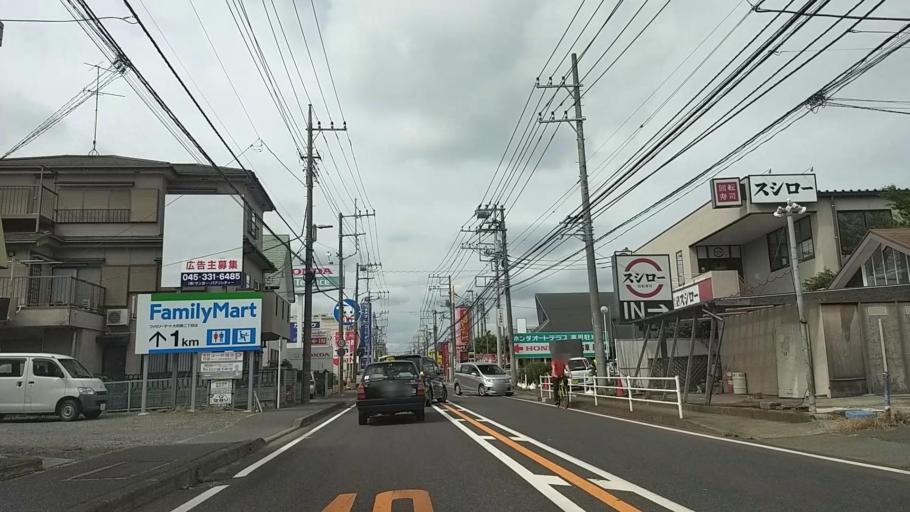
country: JP
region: Kanagawa
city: Minami-rinkan
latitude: 35.4543
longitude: 139.4668
